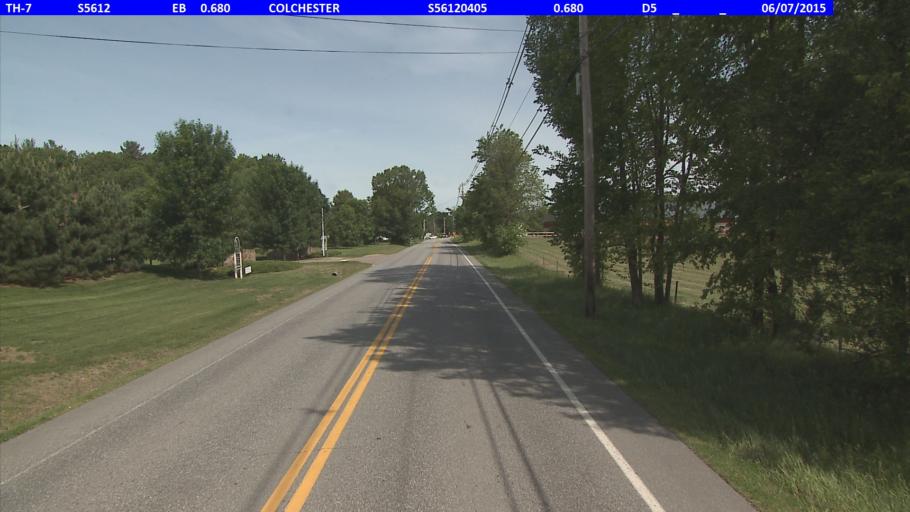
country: US
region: Vermont
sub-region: Chittenden County
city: Colchester
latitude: 44.5197
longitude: -73.1498
